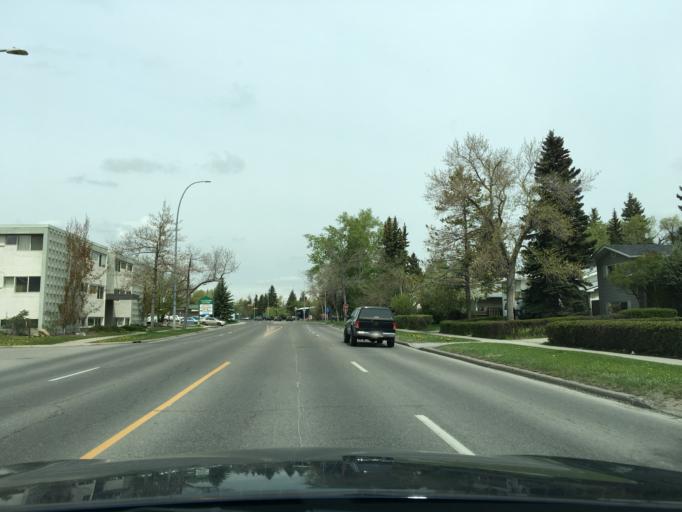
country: CA
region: Alberta
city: Calgary
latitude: 50.9772
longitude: -114.0837
